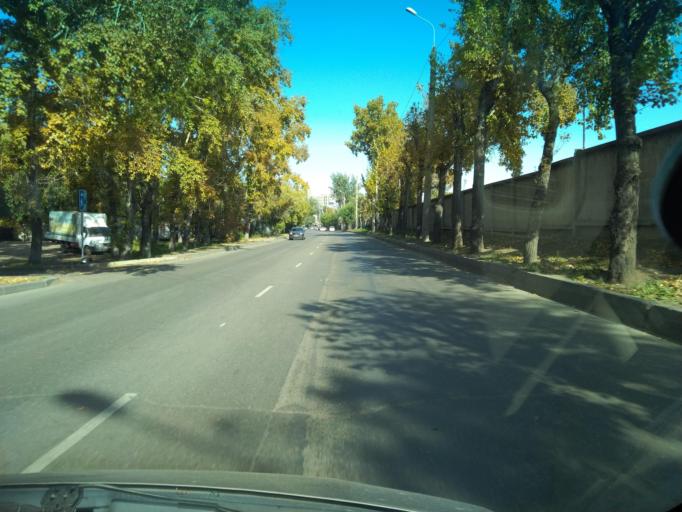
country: RU
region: Krasnoyarskiy
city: Krasnoyarsk
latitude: 56.0074
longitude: 92.9703
